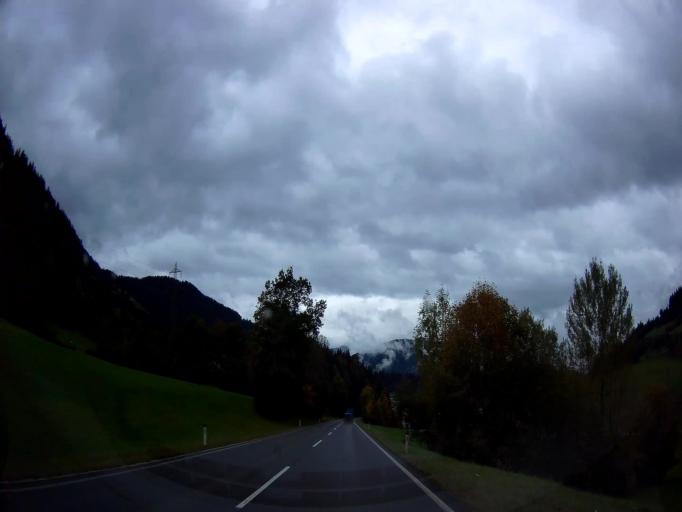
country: AT
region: Tyrol
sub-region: Politischer Bezirk Kufstein
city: Soll
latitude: 47.4902
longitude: 12.1662
